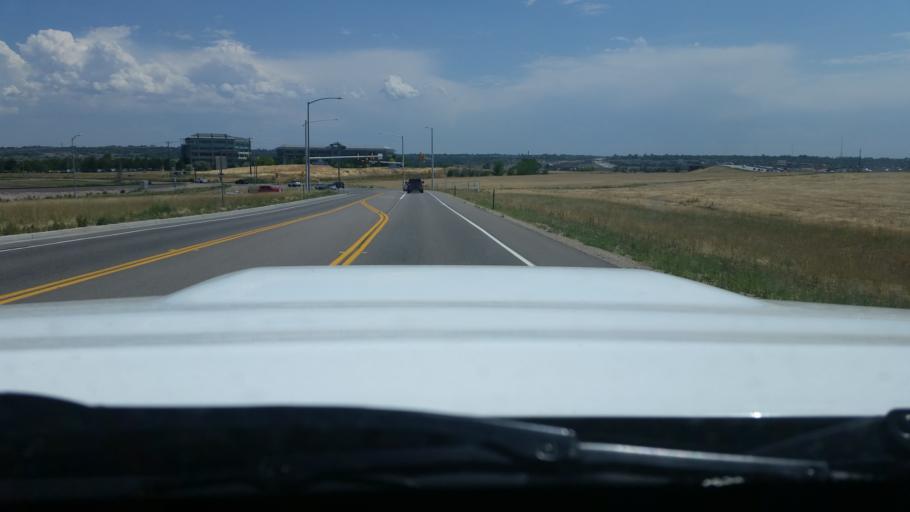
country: US
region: Colorado
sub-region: Broomfield County
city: Broomfield
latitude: 39.9011
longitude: -105.0795
